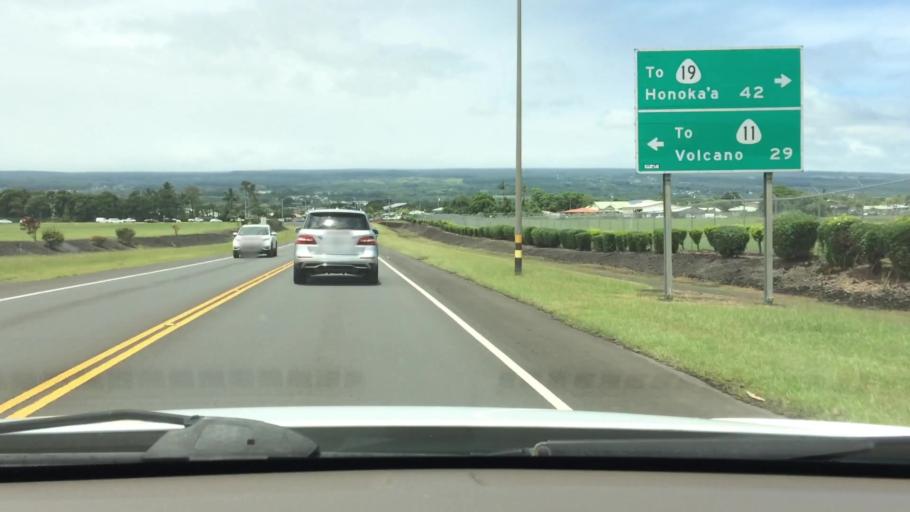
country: US
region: Hawaii
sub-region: Hawaii County
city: Hilo
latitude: 19.7130
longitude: -155.0606
